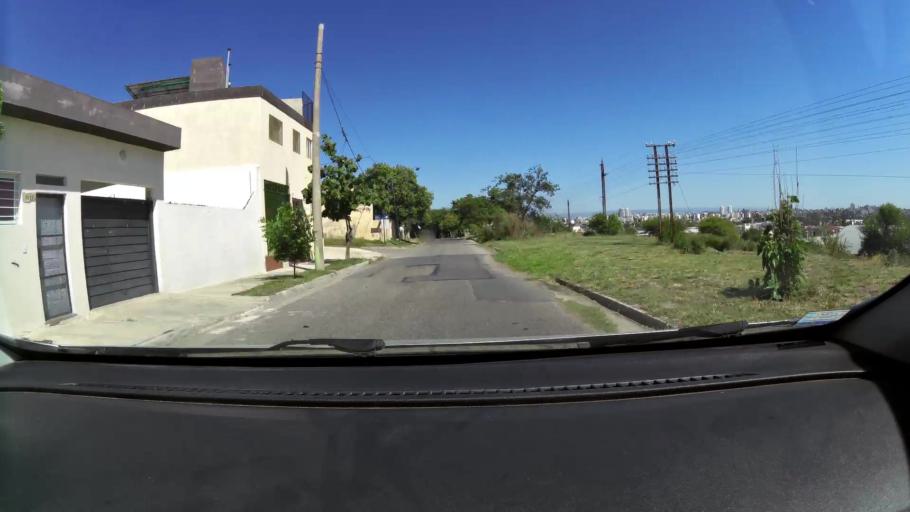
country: AR
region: Cordoba
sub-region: Departamento de Capital
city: Cordoba
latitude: -31.4280
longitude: -64.1545
